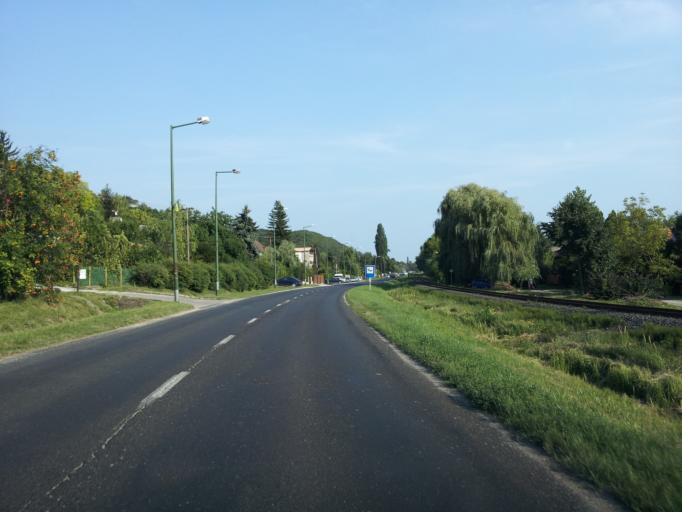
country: HU
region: Veszprem
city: Balatonalmadi
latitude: 47.0567
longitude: 18.0499
